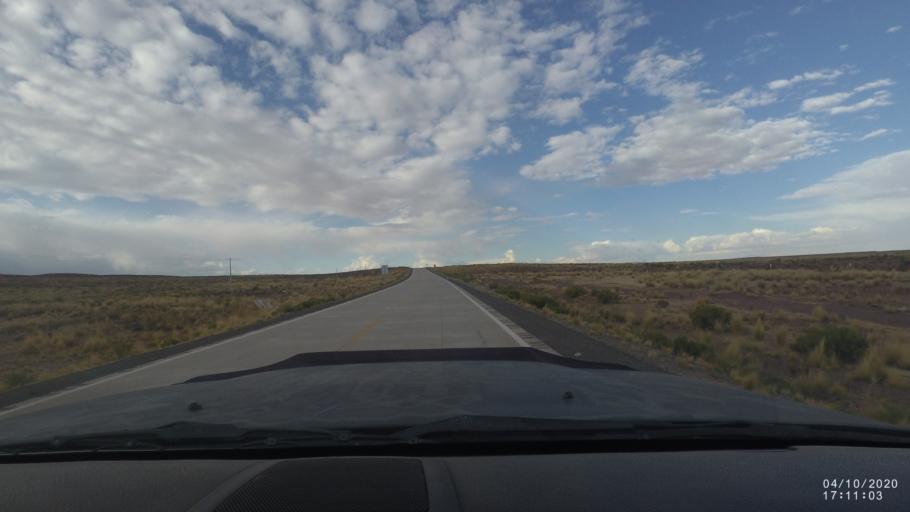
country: BO
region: Oruro
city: Oruro
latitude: -18.3242
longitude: -67.5790
